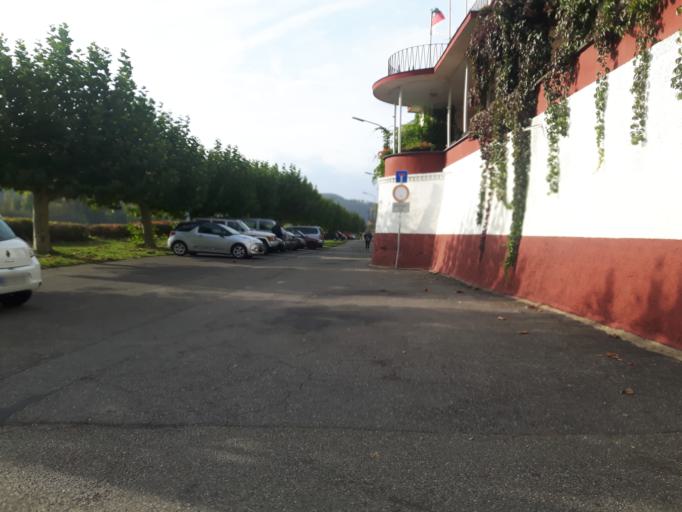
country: DE
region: Rheinland-Pfalz
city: Leutesdorf
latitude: 50.4509
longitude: 7.3831
